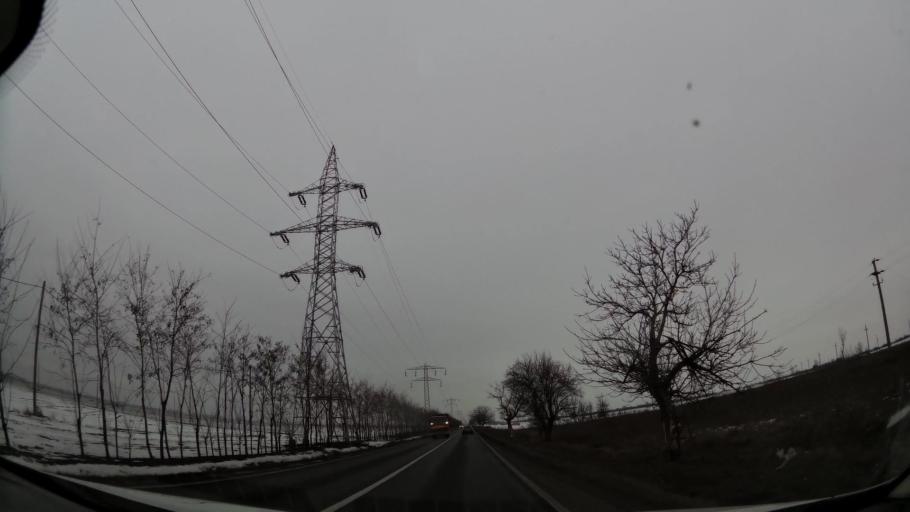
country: RO
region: Dambovita
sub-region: Comuna Salcioara
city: Salcioara
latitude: 44.7216
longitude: 25.6113
